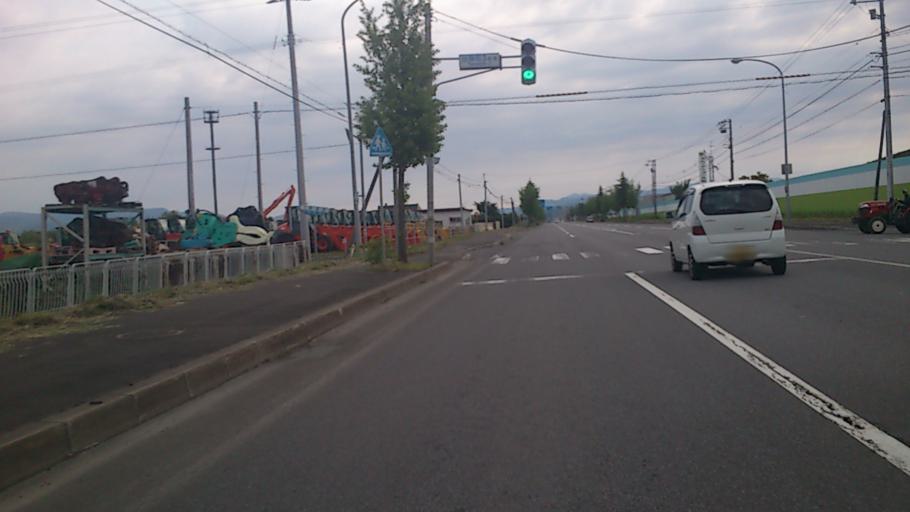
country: JP
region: Hokkaido
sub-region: Asahikawa-shi
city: Asahikawa
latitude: 43.8413
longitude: 142.4831
